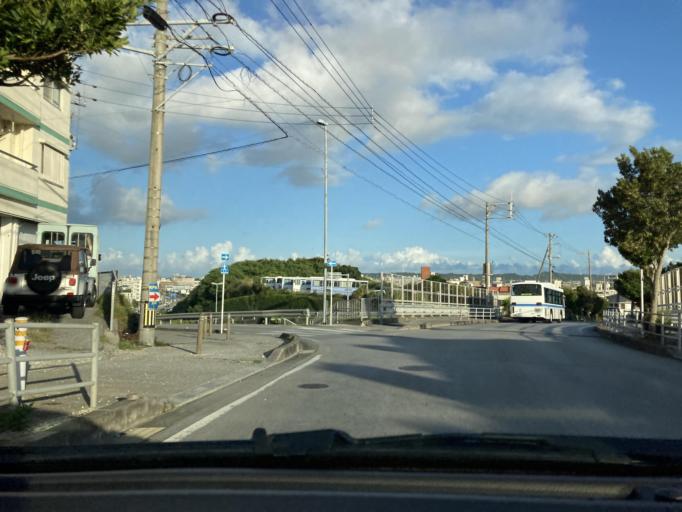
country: JP
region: Okinawa
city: Naha-shi
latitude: 26.2045
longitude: 127.7186
